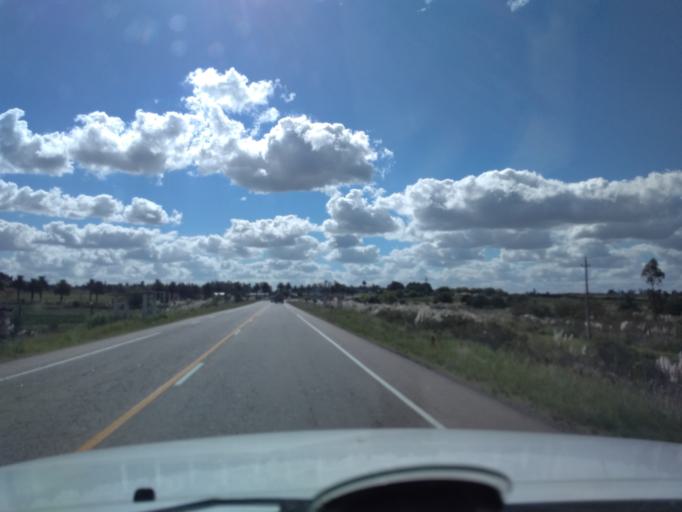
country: UY
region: Canelones
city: Sauce
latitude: -34.6717
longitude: -56.0533
